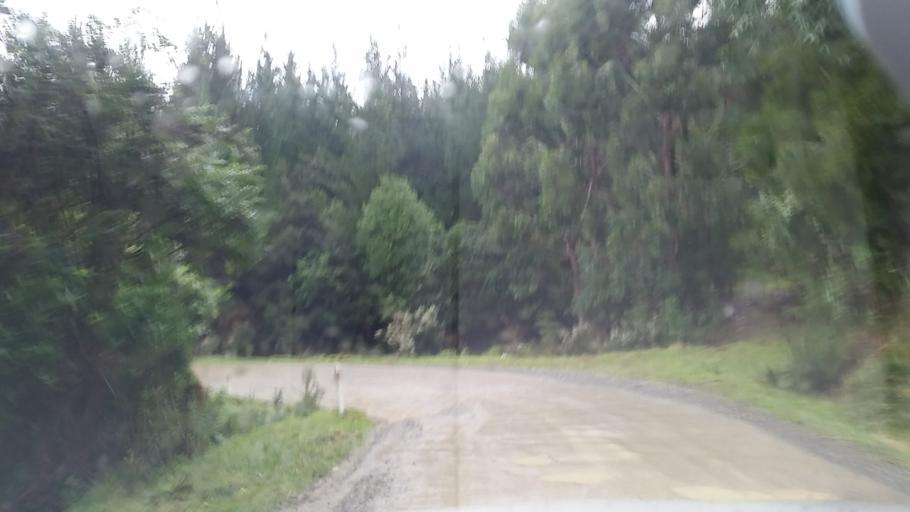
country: NZ
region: Marlborough
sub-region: Marlborough District
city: Picton
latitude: -41.1774
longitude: 174.0719
